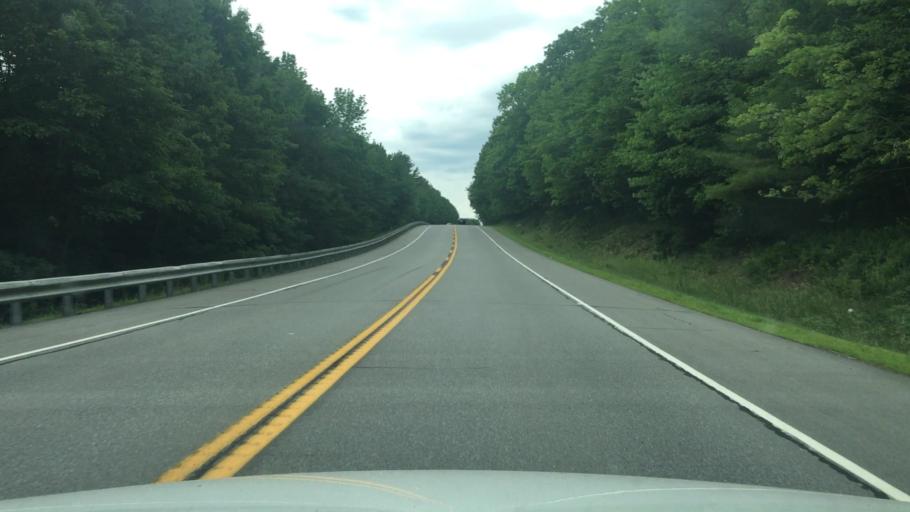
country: US
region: Maine
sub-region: Kennebec County
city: Windsor
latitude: 44.3697
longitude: -69.6312
